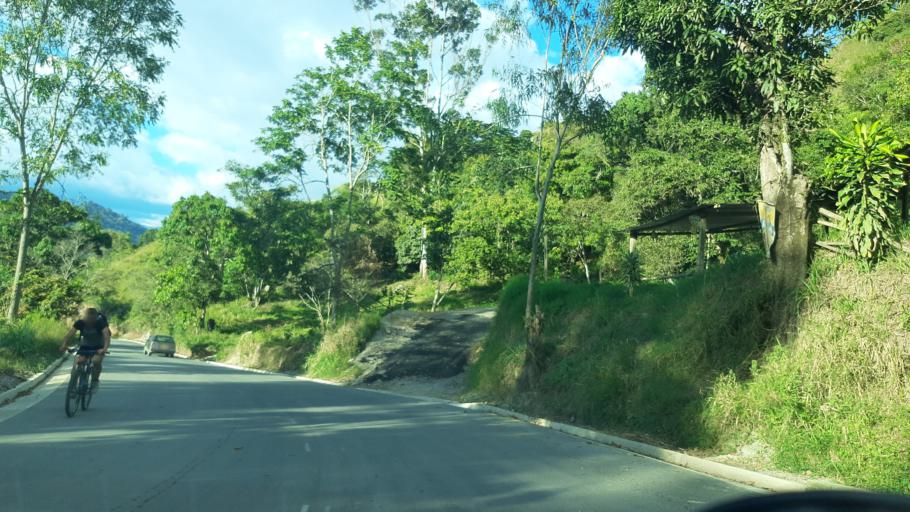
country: CO
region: Boyaca
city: Garagoa
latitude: 5.0797
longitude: -73.3811
